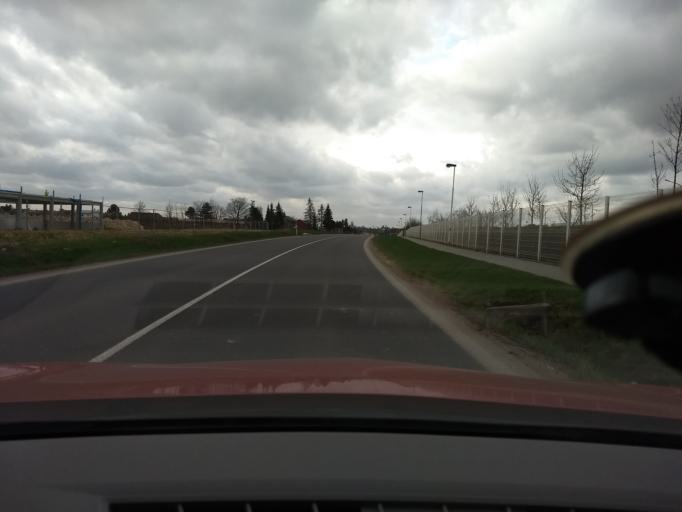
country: CZ
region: Central Bohemia
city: Unhost'
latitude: 50.1212
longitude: 14.1281
